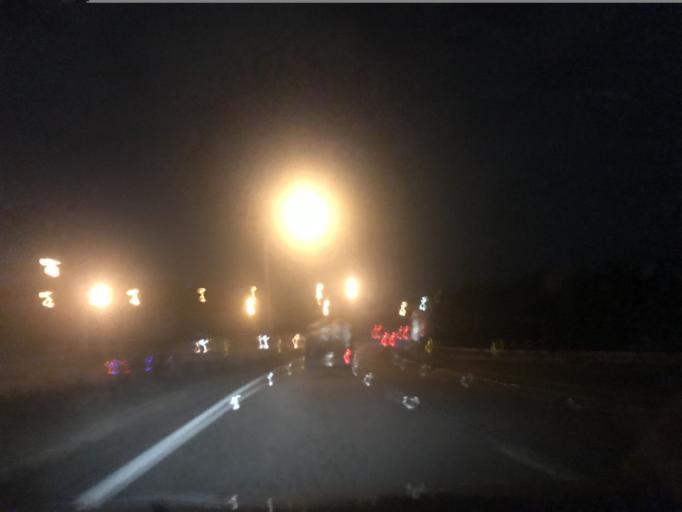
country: TW
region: Taiwan
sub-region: Hsinchu
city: Hsinchu
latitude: 24.7599
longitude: 120.9920
